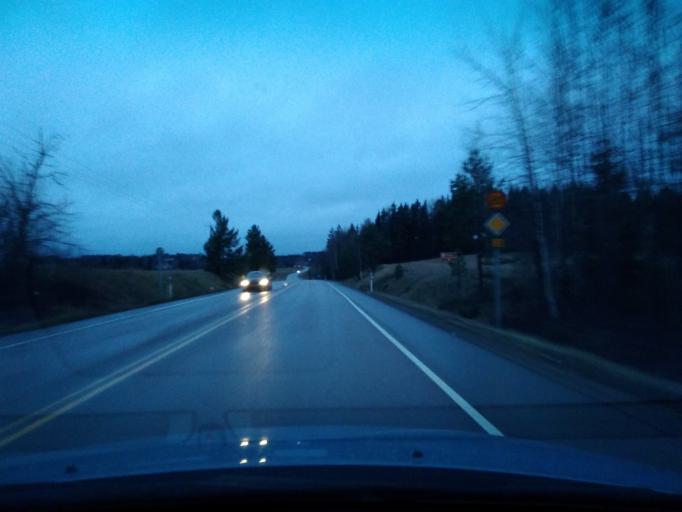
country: FI
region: Uusimaa
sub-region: Porvoo
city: Askola
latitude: 60.4496
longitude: 25.5851
